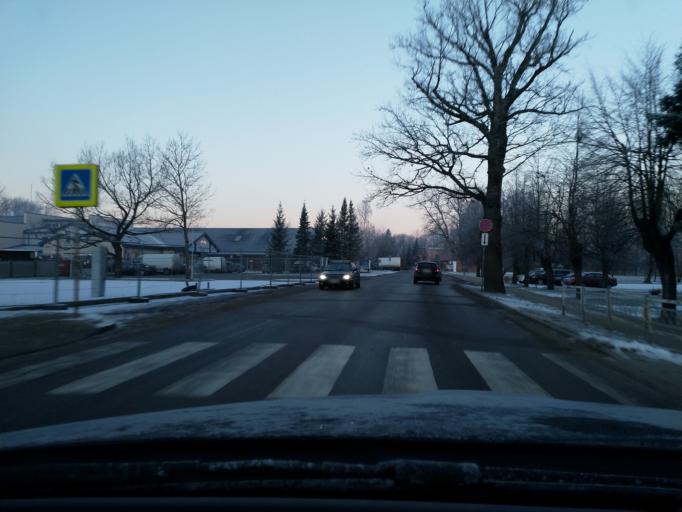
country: LV
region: Kuldigas Rajons
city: Kuldiga
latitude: 56.9624
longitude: 21.9831
